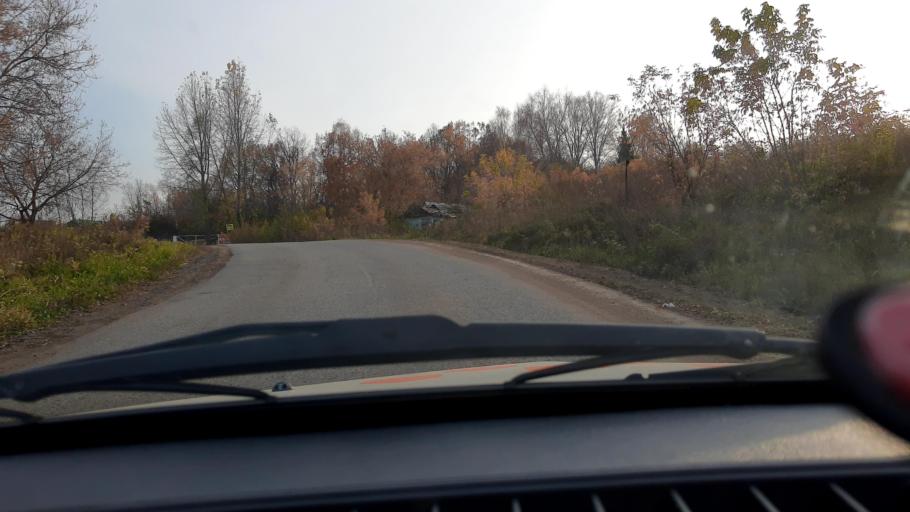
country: RU
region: Bashkortostan
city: Iglino
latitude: 54.7989
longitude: 56.3138
